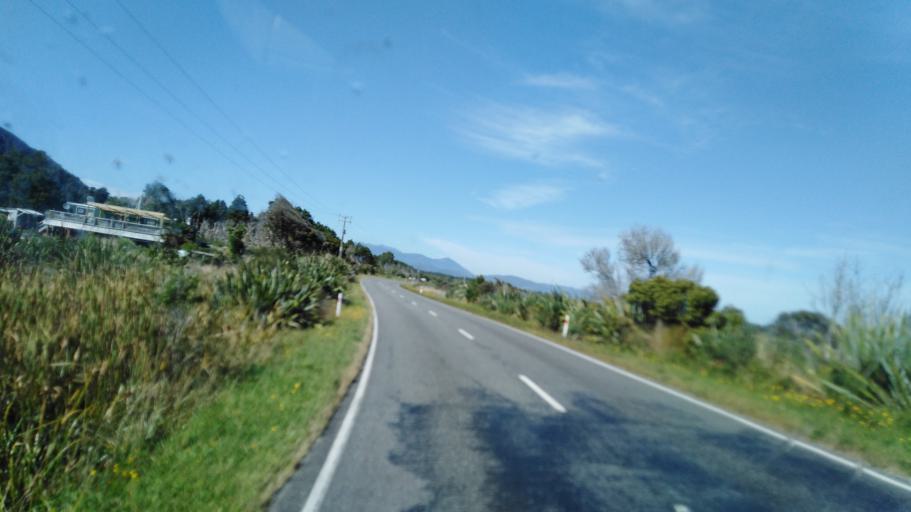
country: NZ
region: West Coast
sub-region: Buller District
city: Westport
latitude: -41.2836
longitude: 172.1043
